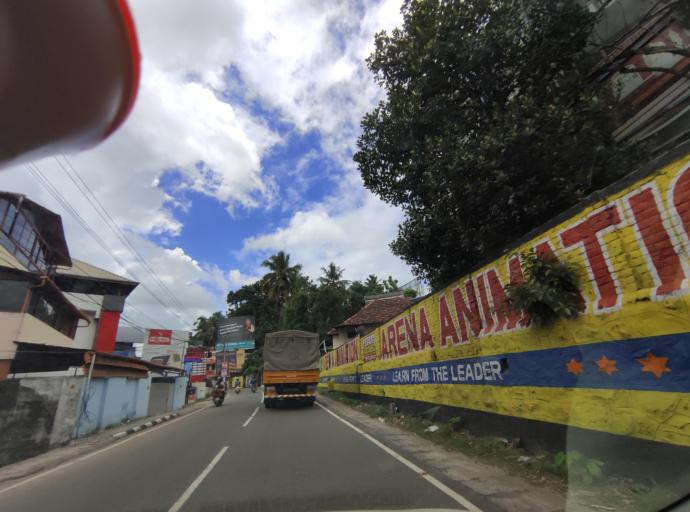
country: IN
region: Kerala
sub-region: Thiruvananthapuram
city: Thiruvananthapuram
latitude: 8.5134
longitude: 76.9472
